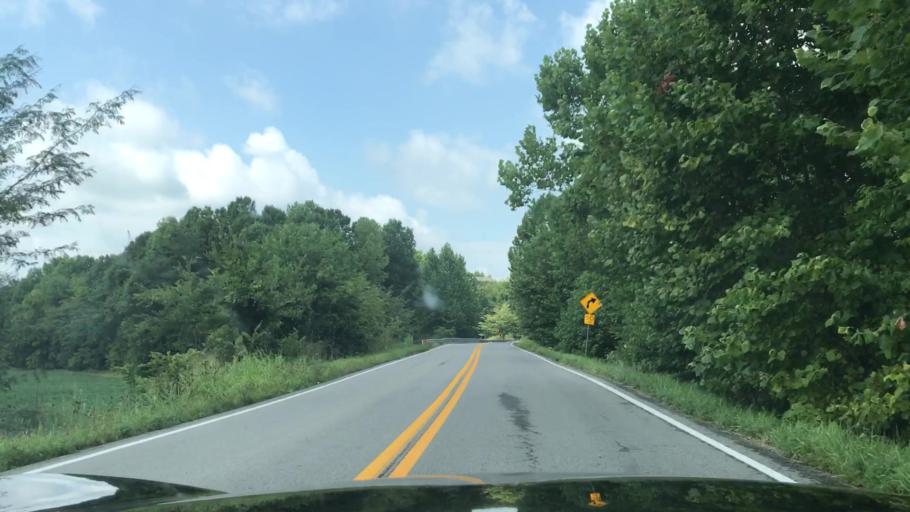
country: US
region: Kentucky
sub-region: Ohio County
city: Beaver Dam
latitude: 37.2133
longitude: -86.9118
